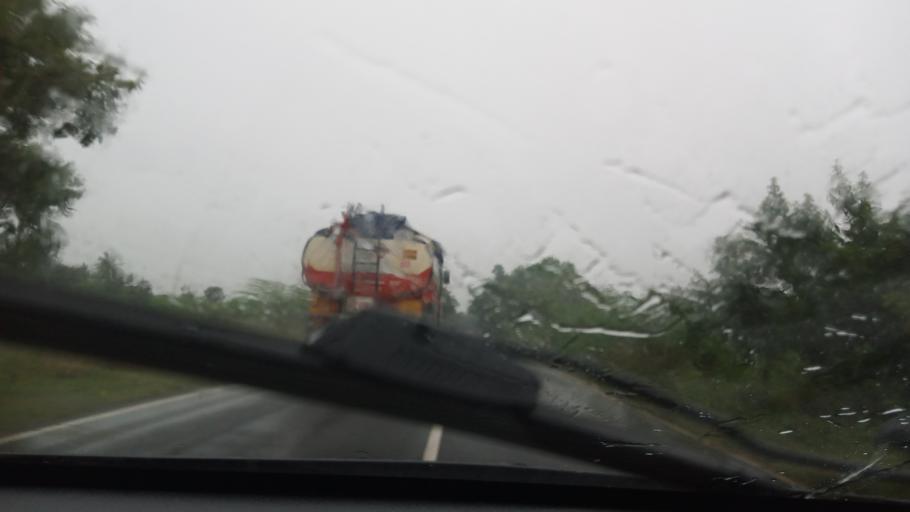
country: IN
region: Tamil Nadu
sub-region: Vellore
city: Kalavai
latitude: 12.8231
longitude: 79.4088
